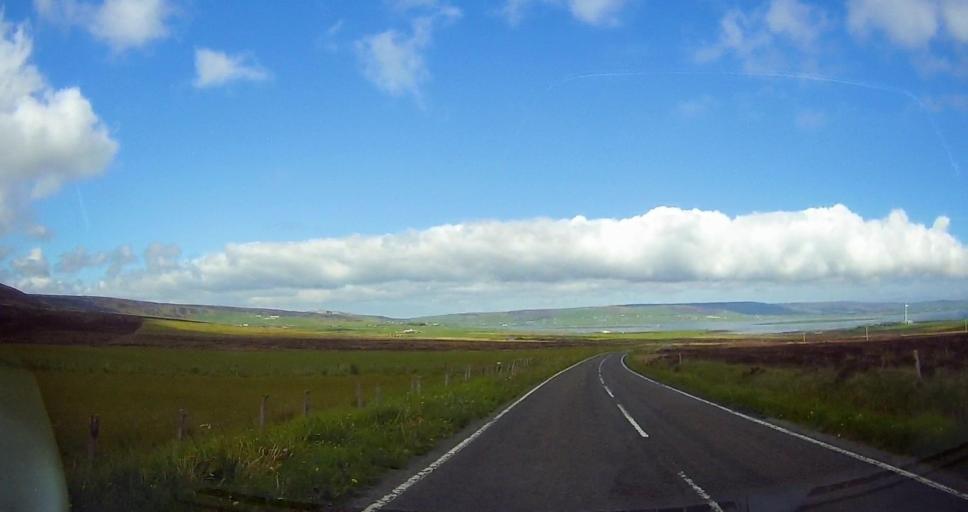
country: GB
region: Scotland
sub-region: Orkney Islands
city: Orkney
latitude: 58.9830
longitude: -3.0437
